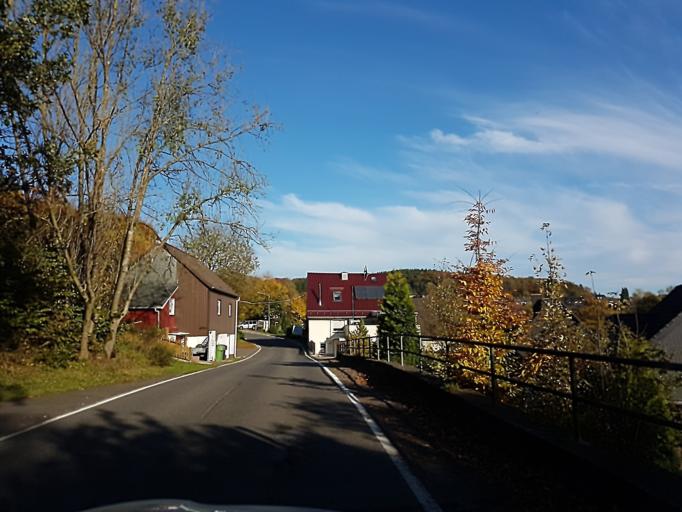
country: DE
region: North Rhine-Westphalia
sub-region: Regierungsbezirk Koln
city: Marienheide
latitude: 51.0906
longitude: 7.5311
